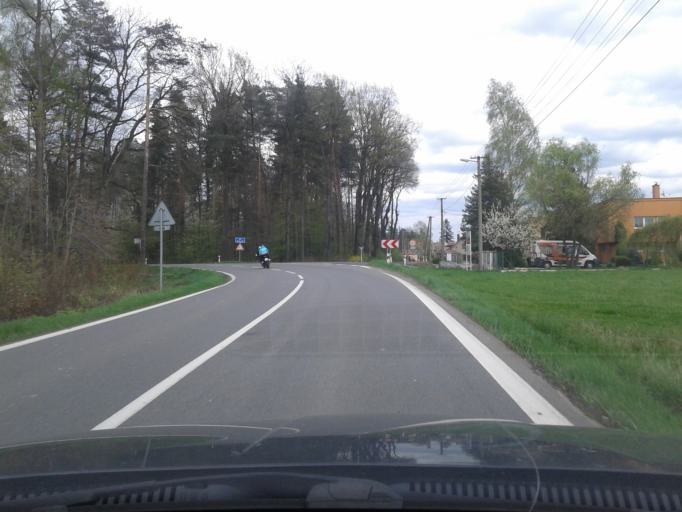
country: CZ
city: Vaclavovice
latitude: 49.7443
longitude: 18.3741
